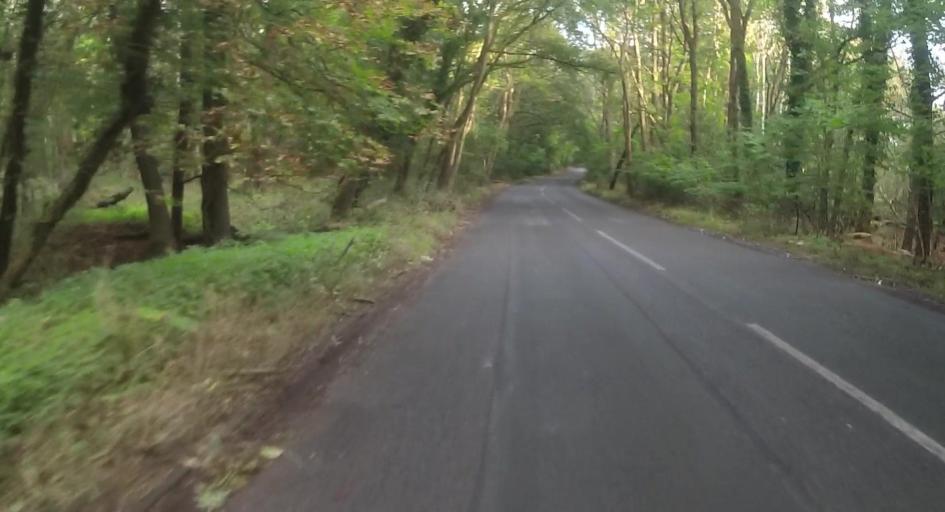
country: GB
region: England
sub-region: Hampshire
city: Tadley
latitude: 51.3792
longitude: -1.1351
